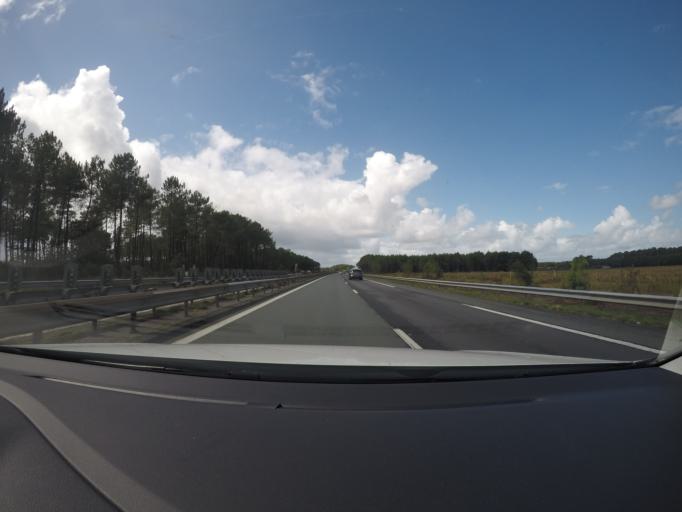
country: FR
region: Aquitaine
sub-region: Departement des Landes
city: Saint-Vincent-de-Tyrosse
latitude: 43.6808
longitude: -1.2916
